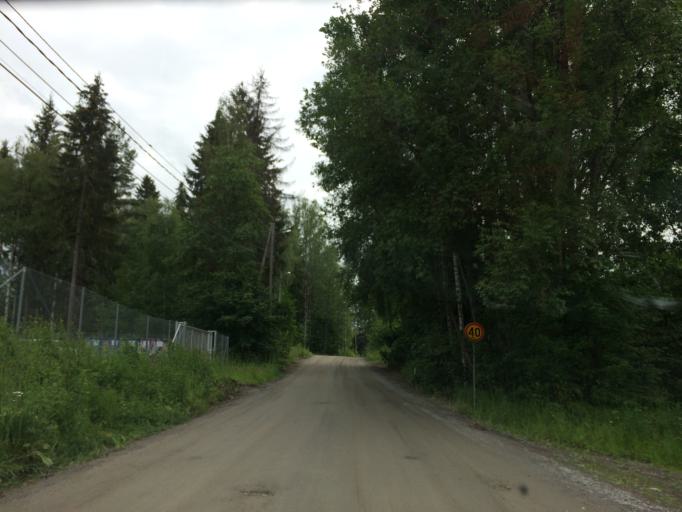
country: FI
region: Haeme
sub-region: Haemeenlinna
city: Haemeenlinna
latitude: 60.9742
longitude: 24.5214
